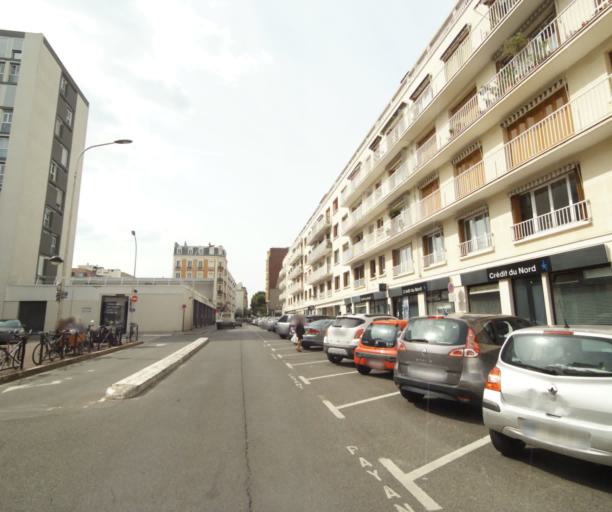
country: FR
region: Ile-de-France
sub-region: Departement des Hauts-de-Seine
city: Bois-Colombes
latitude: 48.9153
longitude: 2.2727
